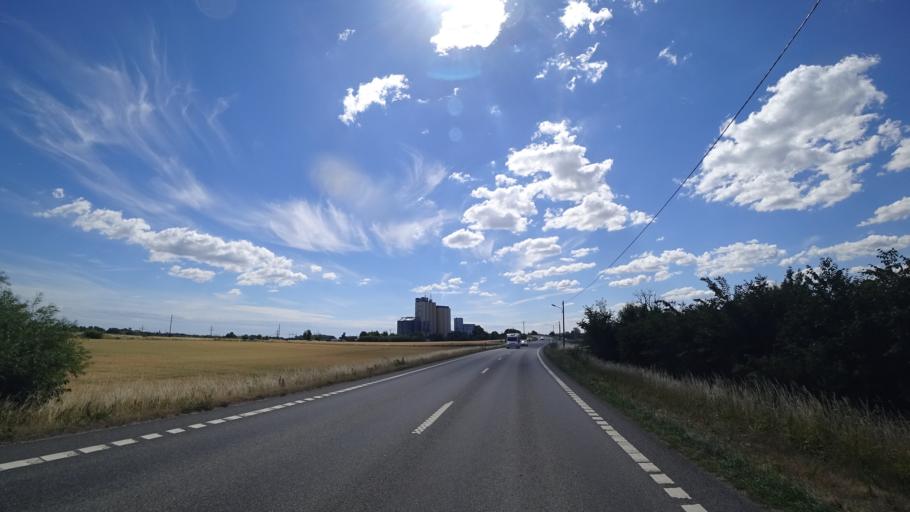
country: SE
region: Skane
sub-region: Kristianstads Kommun
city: Kristianstad
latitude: 56.0439
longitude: 14.0896
